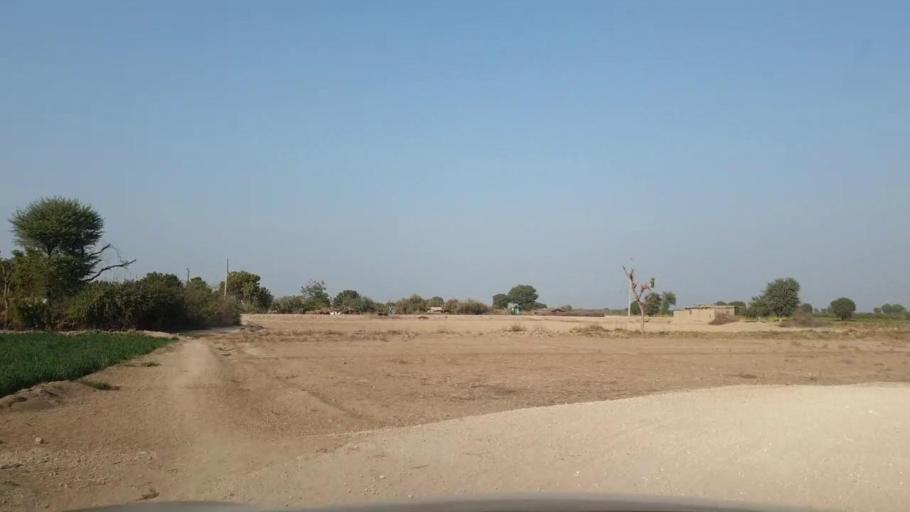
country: PK
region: Sindh
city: Tando Allahyar
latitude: 25.5696
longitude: 68.7942
